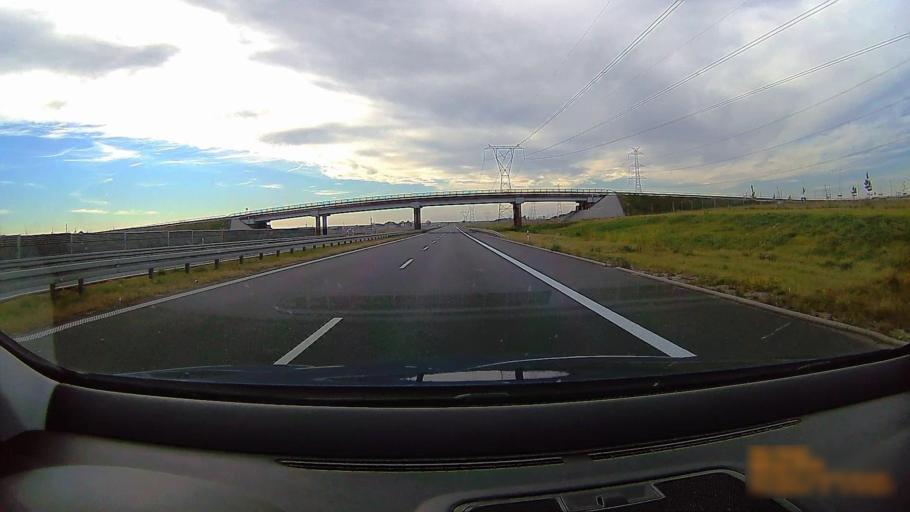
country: PL
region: Greater Poland Voivodeship
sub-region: Powiat ostrowski
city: Przygodzice
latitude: 51.6154
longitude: 17.8604
